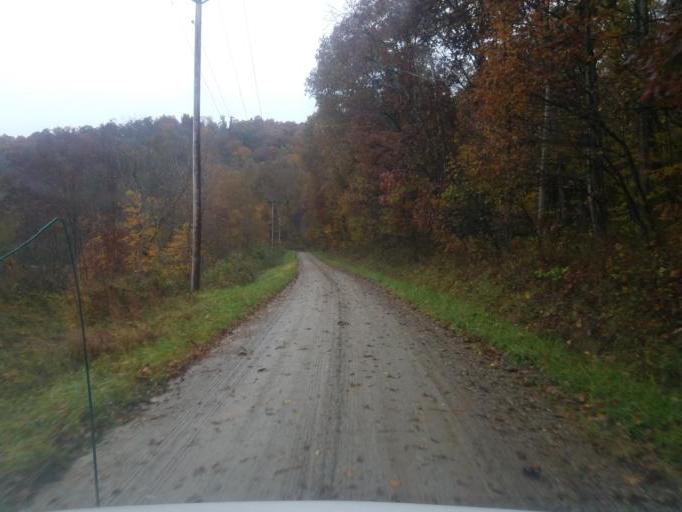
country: US
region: Ohio
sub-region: Washington County
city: Beverly
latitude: 39.4653
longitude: -81.7641
